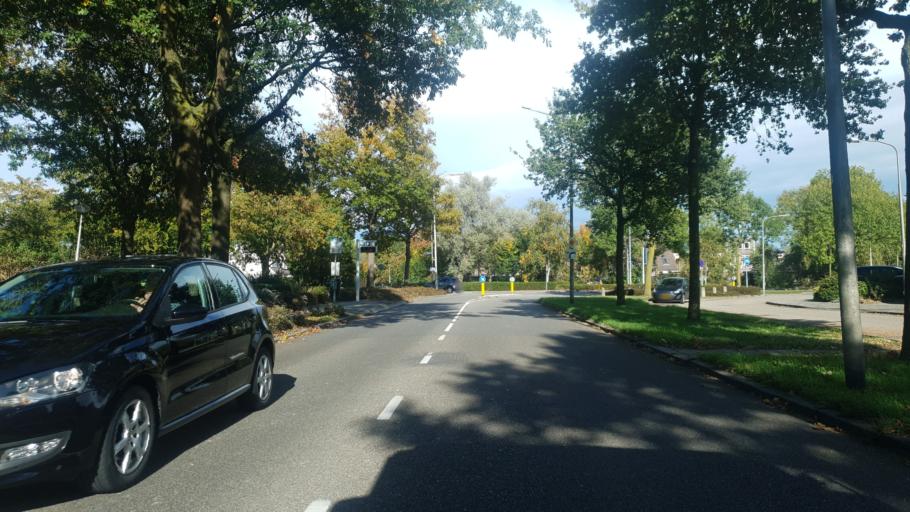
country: NL
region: Gelderland
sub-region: Gemeente Nijmegen
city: Lindenholt
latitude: 51.8353
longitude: 5.7850
